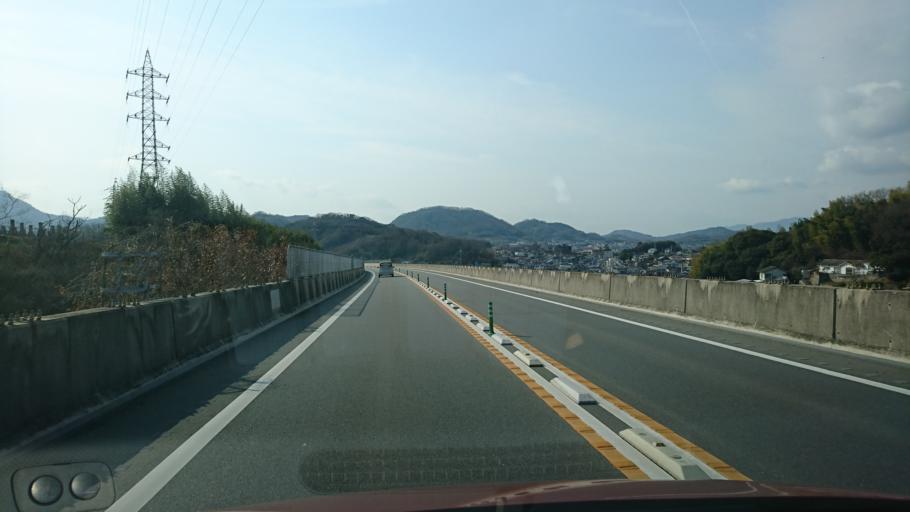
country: JP
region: Hiroshima
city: Onomichi
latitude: 34.4019
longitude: 133.2106
